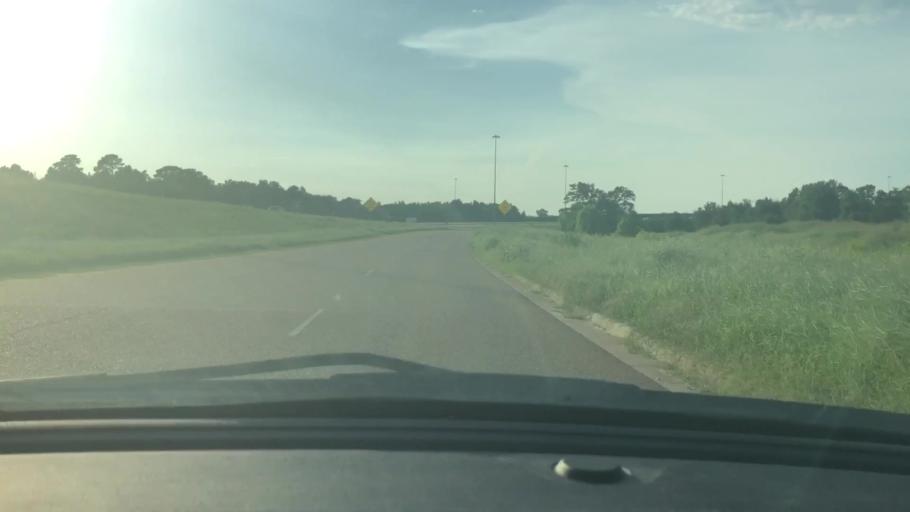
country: US
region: Texas
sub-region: Bowie County
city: Wake Village
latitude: 33.3878
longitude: -94.0934
